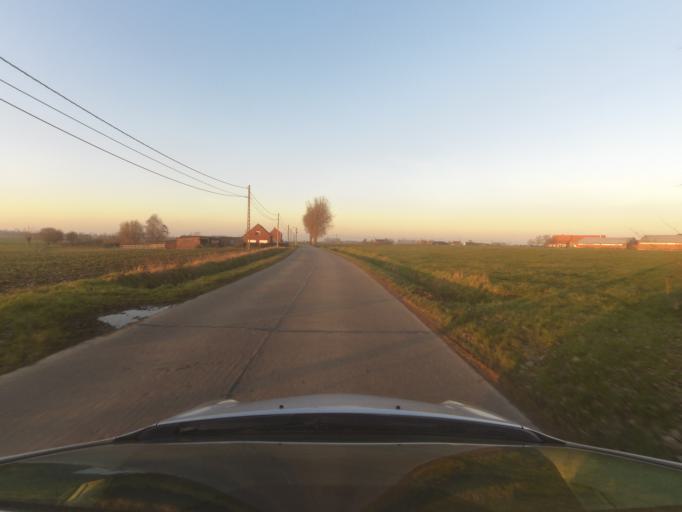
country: BE
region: Flanders
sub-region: Provincie West-Vlaanderen
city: Ieper
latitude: 50.8928
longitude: 2.8189
